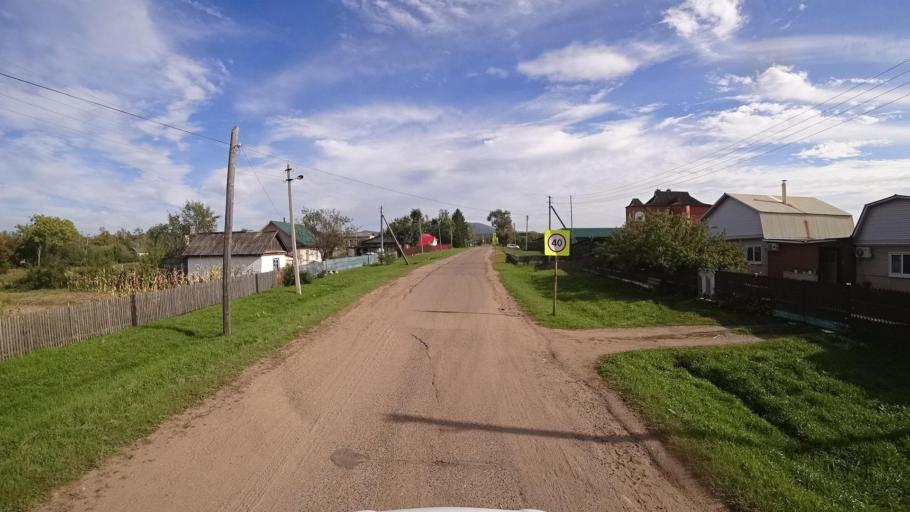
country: RU
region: Primorskiy
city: Dostoyevka
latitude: 44.2983
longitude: 133.4524
